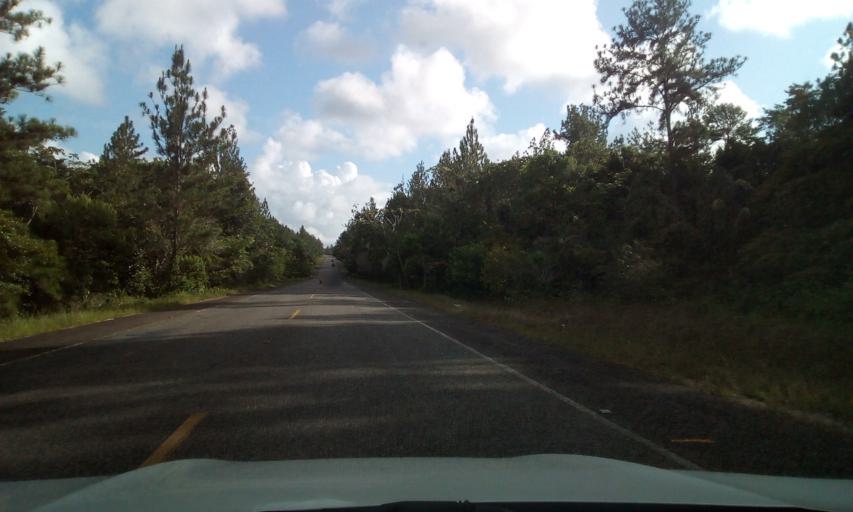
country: BR
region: Bahia
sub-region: Entre Rios
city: Entre Rios
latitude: -12.1481
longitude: -37.7974
